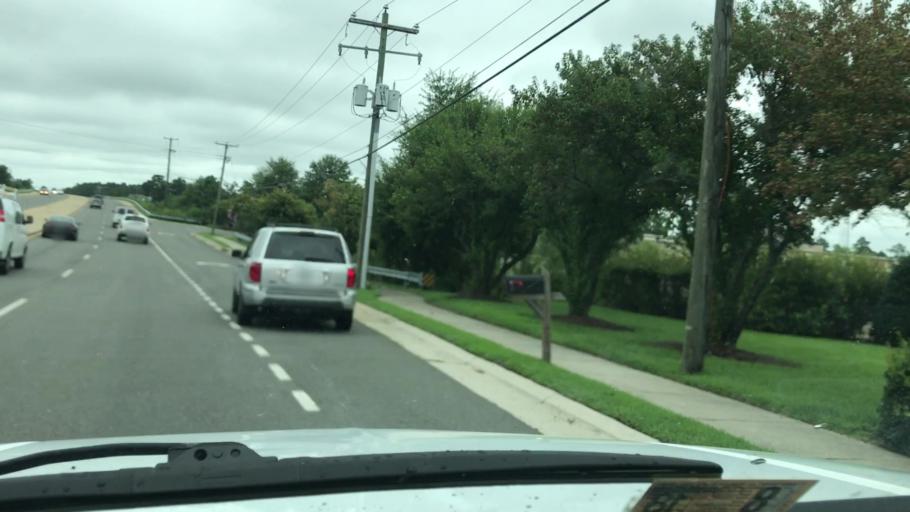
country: US
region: Virginia
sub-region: Henrico County
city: Short Pump
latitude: 37.6539
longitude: -77.6110
